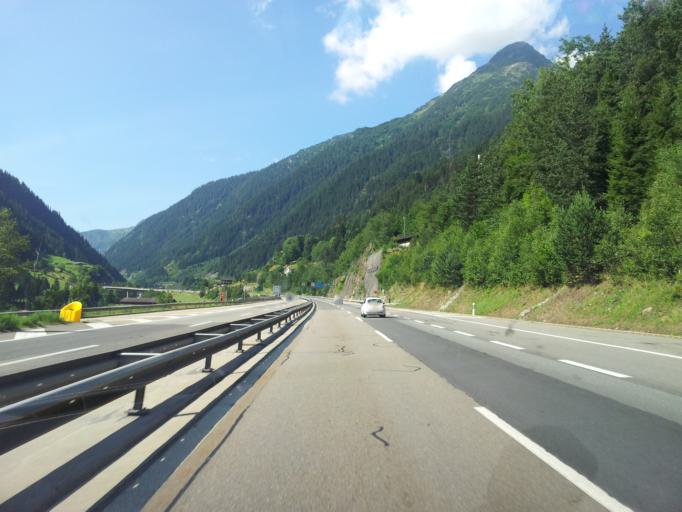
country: CH
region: Uri
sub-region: Uri
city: Andermatt
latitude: 46.7035
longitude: 8.5993
